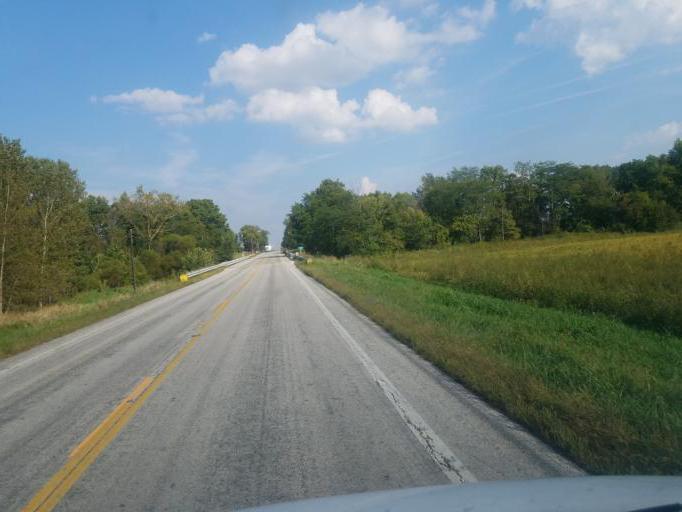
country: US
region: Ohio
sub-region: Hancock County
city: Arlington
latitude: 40.8912
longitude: -83.5656
